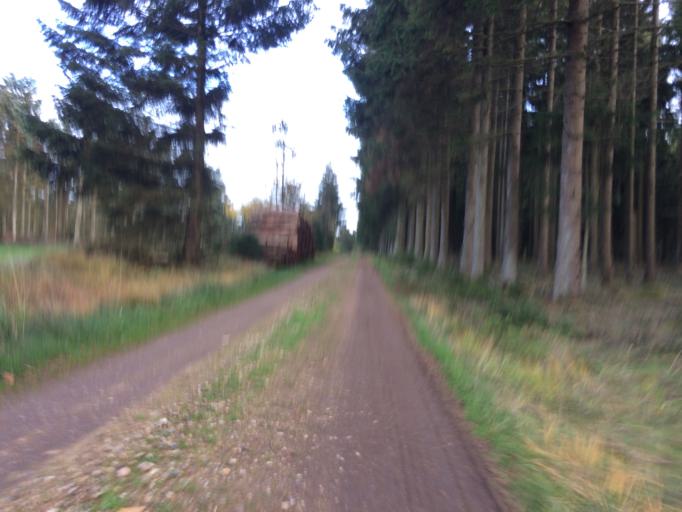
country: DK
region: Central Jutland
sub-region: Holstebro Kommune
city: Ulfborg
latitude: 56.2111
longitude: 8.4614
